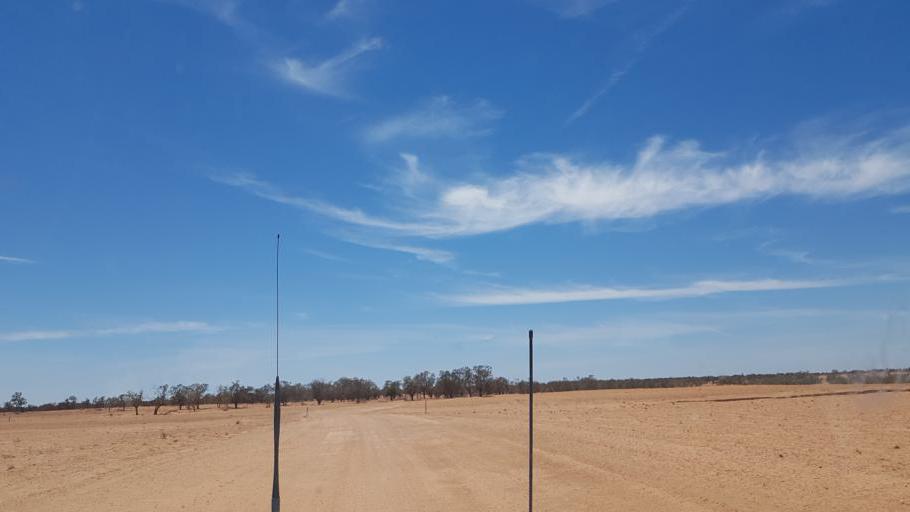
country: AU
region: New South Wales
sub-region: Wentworth
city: Dareton
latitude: -33.3458
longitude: 141.4589
